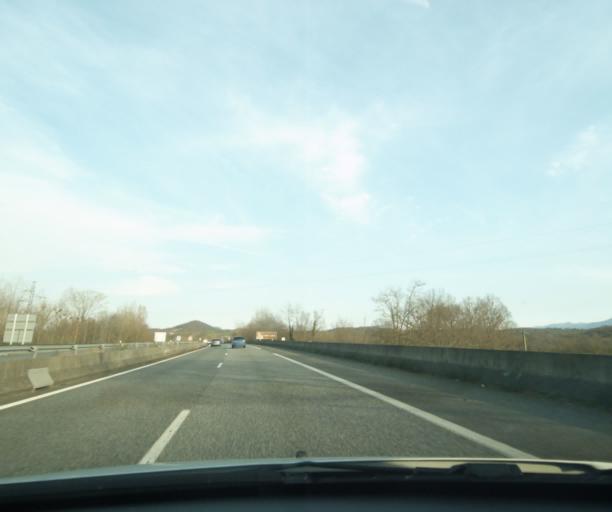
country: FR
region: Midi-Pyrenees
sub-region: Departement de la Haute-Garonne
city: Salies-du-Salat
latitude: 43.1163
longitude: 0.9084
